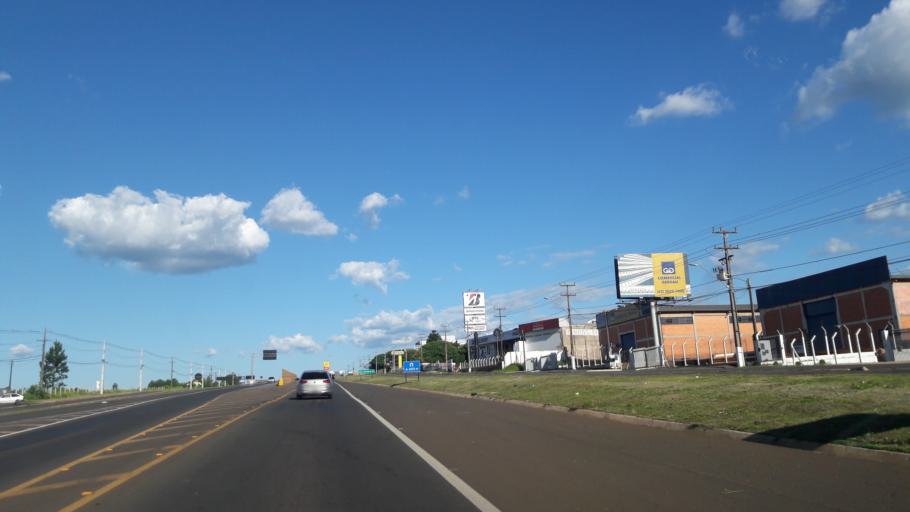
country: BR
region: Parana
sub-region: Guarapuava
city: Guarapuava
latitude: -25.3659
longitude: -51.4875
